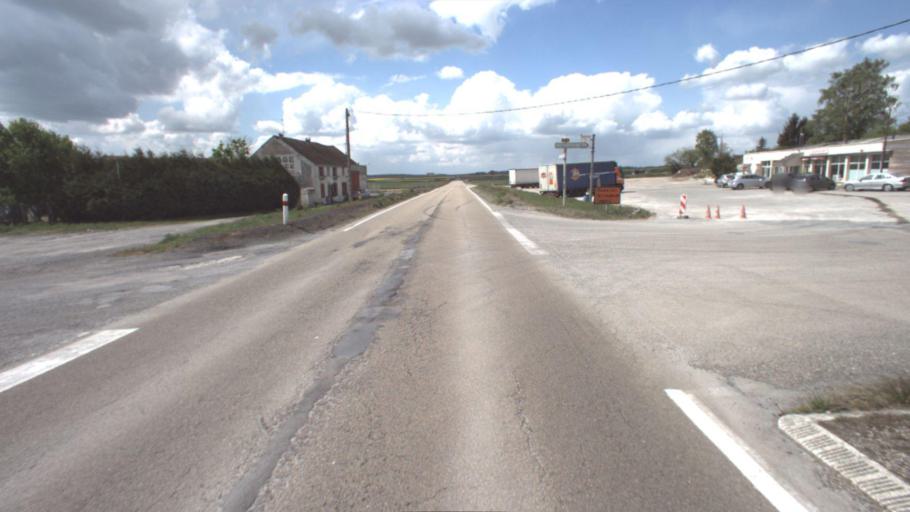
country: FR
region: Ile-de-France
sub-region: Departement de Seine-et-Marne
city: Villiers-Saint-Georges
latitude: 48.6922
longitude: 3.3973
